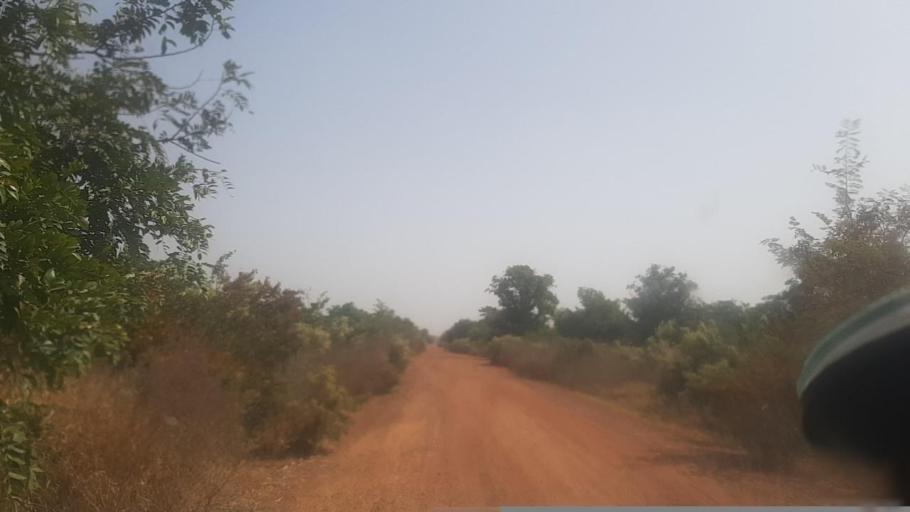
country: ML
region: Segou
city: Bla
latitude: 12.9190
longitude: -6.2562
